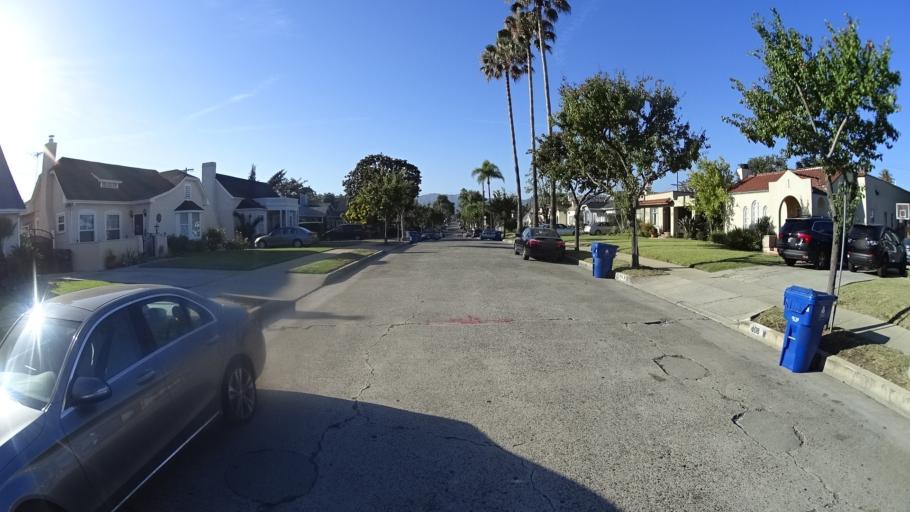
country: US
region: California
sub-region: Los Angeles County
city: Hollywood
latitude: 34.0779
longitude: -118.3227
